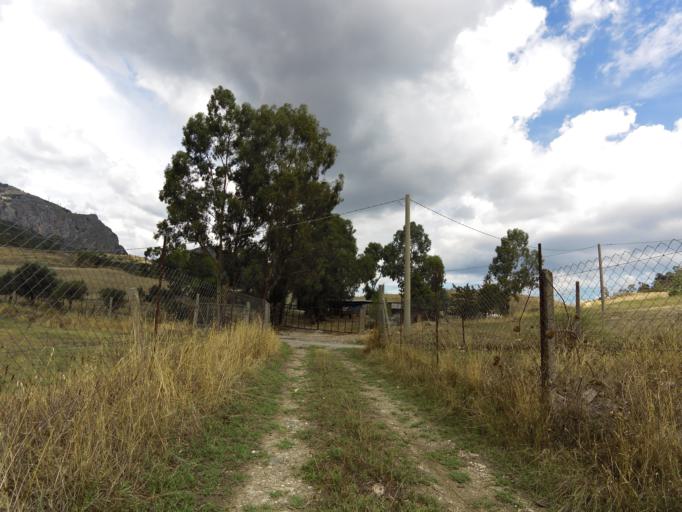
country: IT
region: Calabria
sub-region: Provincia di Reggio Calabria
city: Stilo
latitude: 38.4541
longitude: 16.4693
